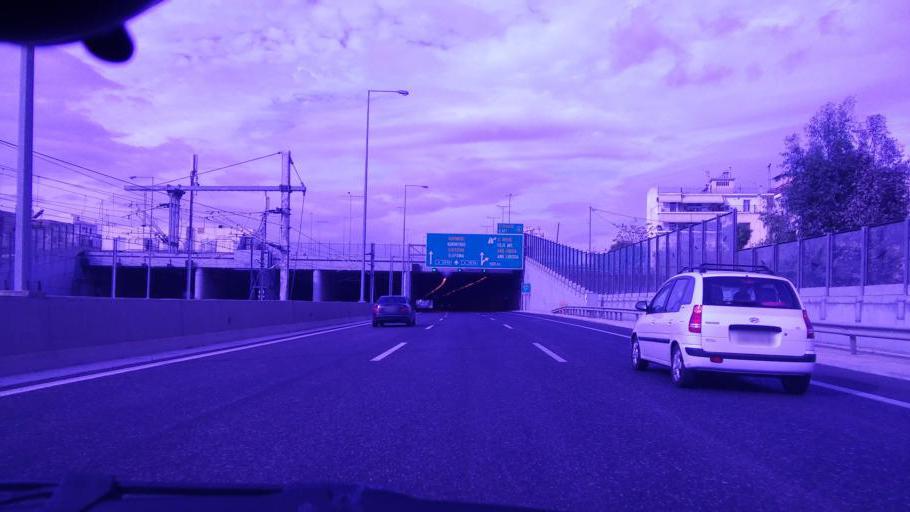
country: GR
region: Attica
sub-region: Nomarchia Dytikis Attikis
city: Zefyri
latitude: 38.0695
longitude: 23.7201
